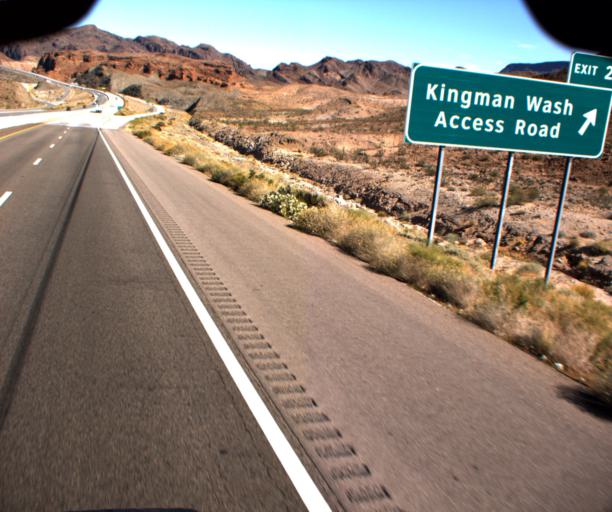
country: US
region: Nevada
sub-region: Clark County
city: Boulder City
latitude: 35.9964
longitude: -114.7195
